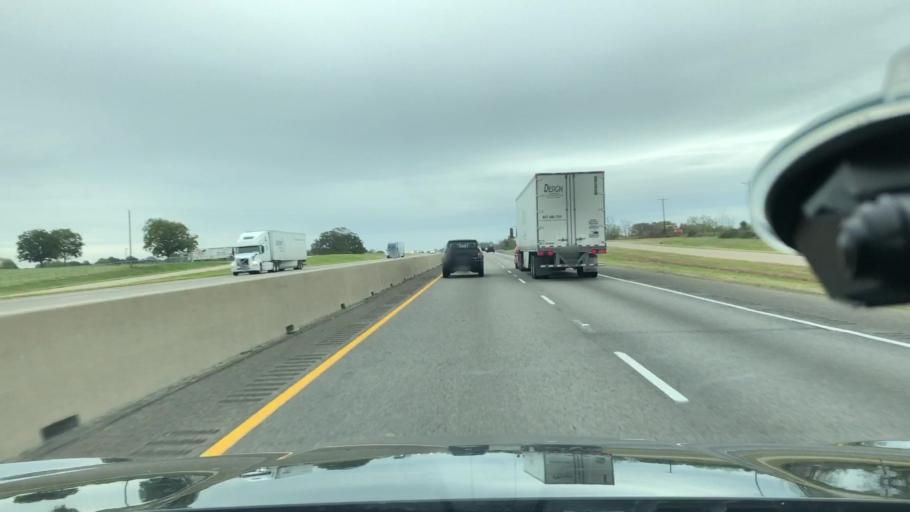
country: US
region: Texas
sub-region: Hopkins County
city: Sulphur Springs
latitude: 33.1472
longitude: -95.5213
